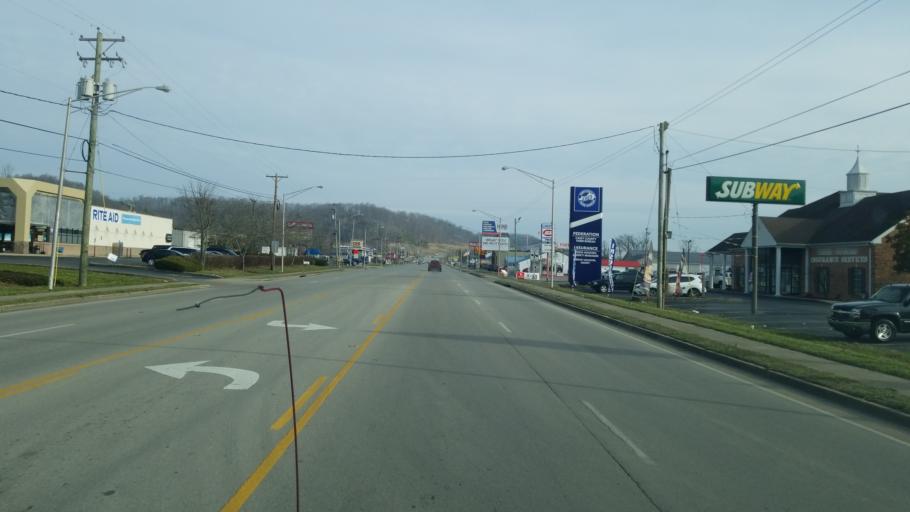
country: US
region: Kentucky
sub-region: Casey County
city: Liberty
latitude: 37.3182
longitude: -84.9293
